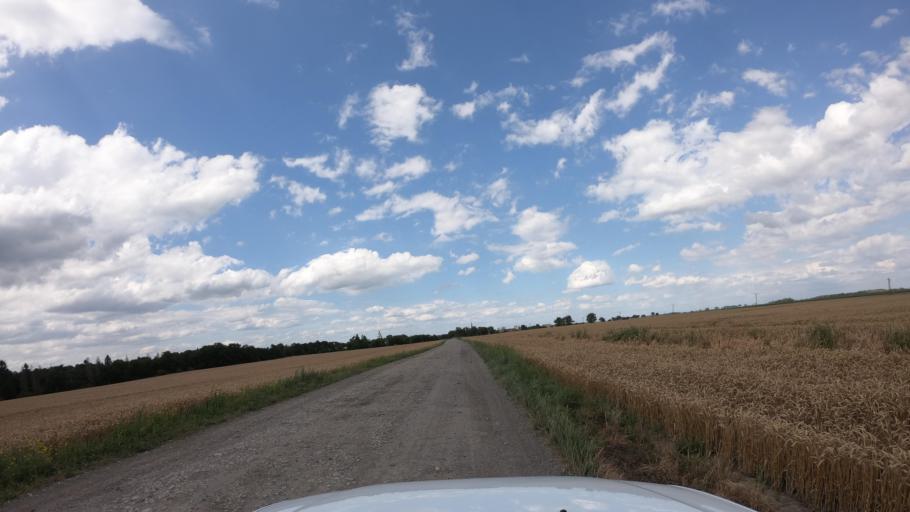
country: PL
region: West Pomeranian Voivodeship
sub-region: Powiat pyrzycki
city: Warnice
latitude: 53.2607
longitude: 14.9104
